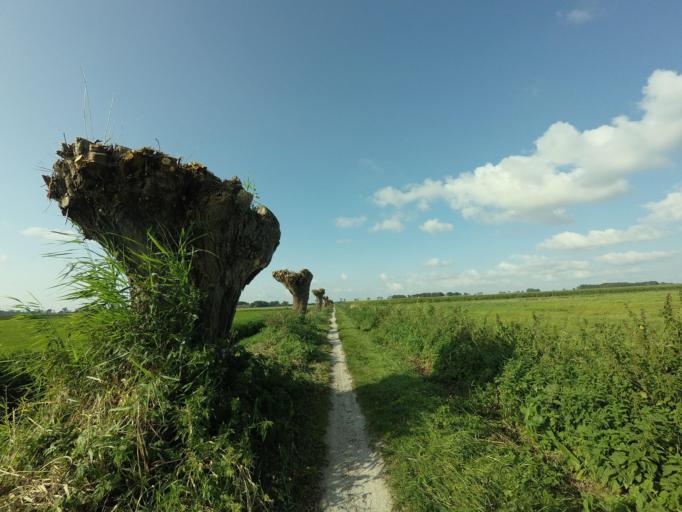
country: NL
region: Flevoland
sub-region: Gemeente Noordoostpolder
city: Ens
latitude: 52.6595
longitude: 5.7752
